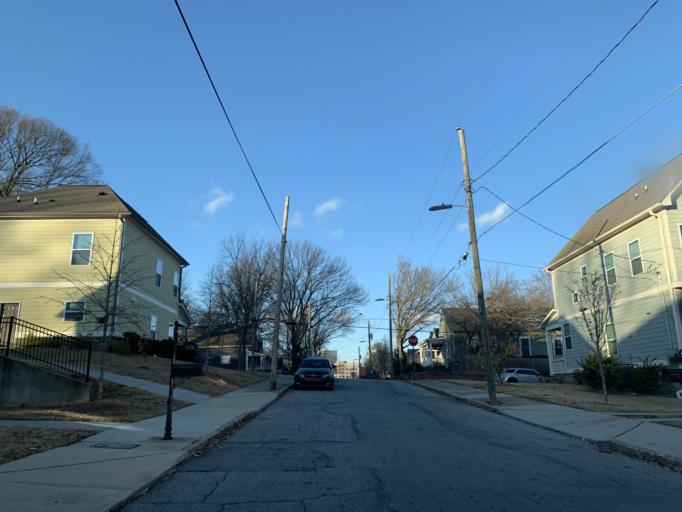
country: US
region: Georgia
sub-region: Fulton County
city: Atlanta
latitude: 33.7376
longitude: -84.3958
